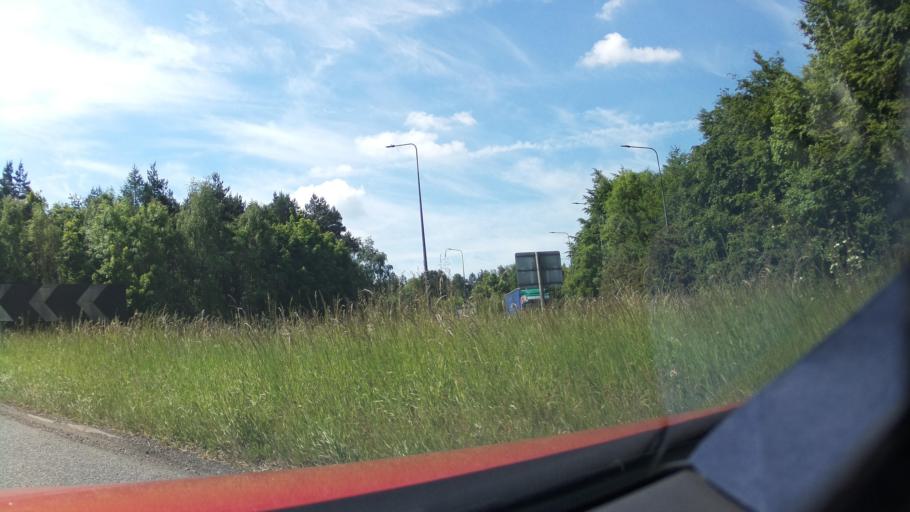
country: GB
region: England
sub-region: North Lincolnshire
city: Scawby
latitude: 53.5457
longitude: -0.5576
